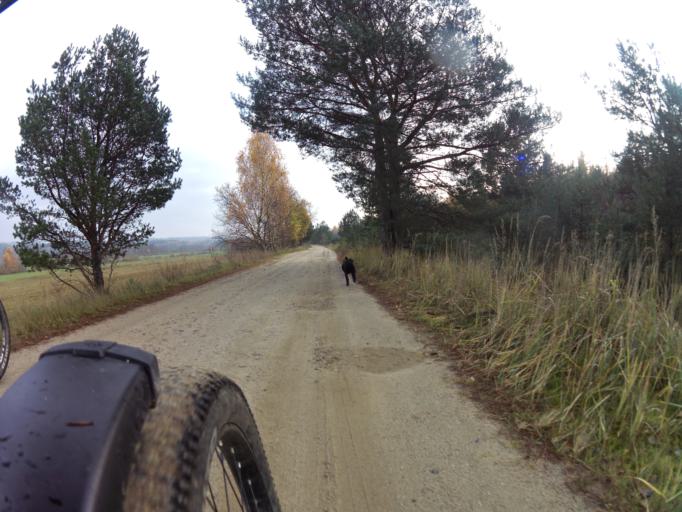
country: PL
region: Pomeranian Voivodeship
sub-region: Powiat wejherowski
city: Gniewino
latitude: 54.7047
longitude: 18.1046
